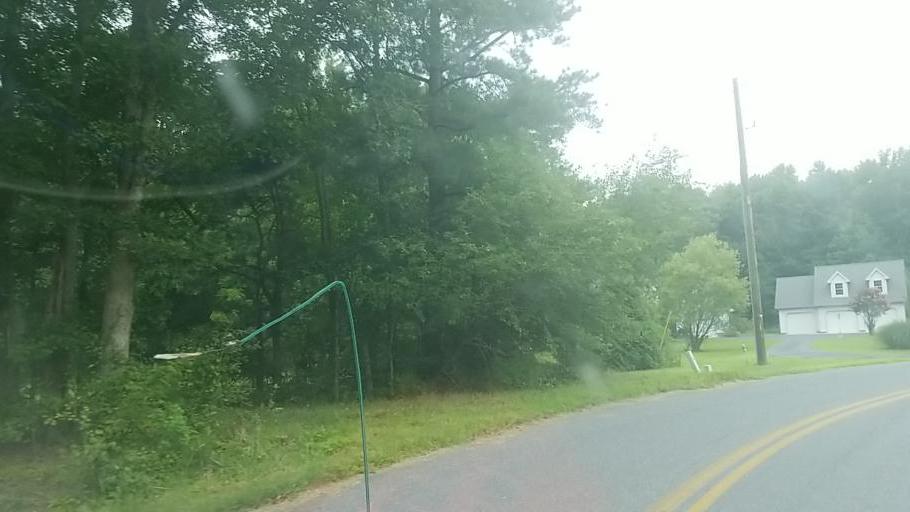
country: US
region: Maryland
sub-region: Worcester County
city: Ocean Pines
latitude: 38.4219
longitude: -75.1910
